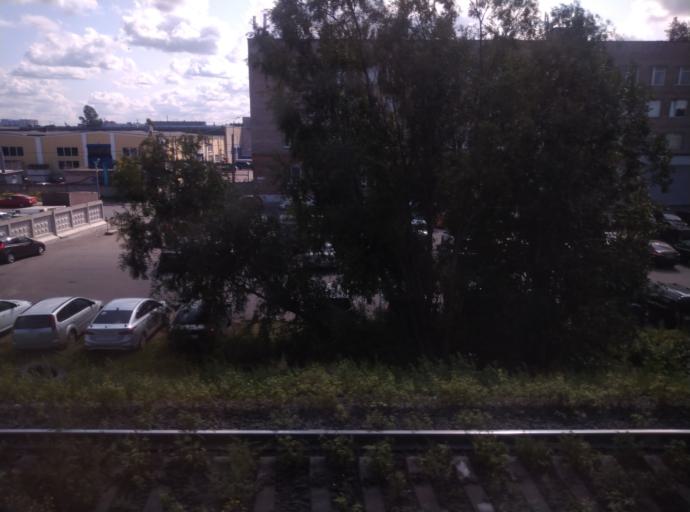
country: RU
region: St.-Petersburg
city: Centralniy
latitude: 59.9083
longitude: 30.3859
